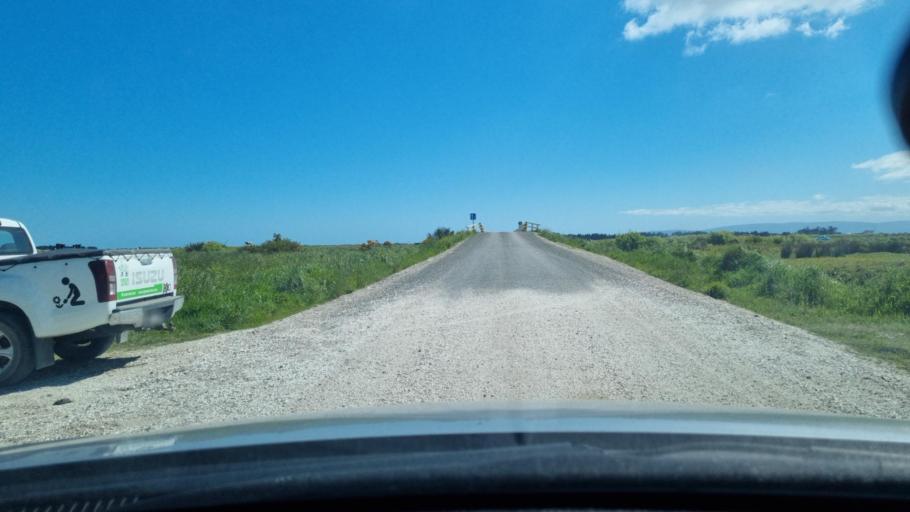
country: NZ
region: Southland
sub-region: Invercargill City
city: Invercargill
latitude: -46.3693
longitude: 168.2518
